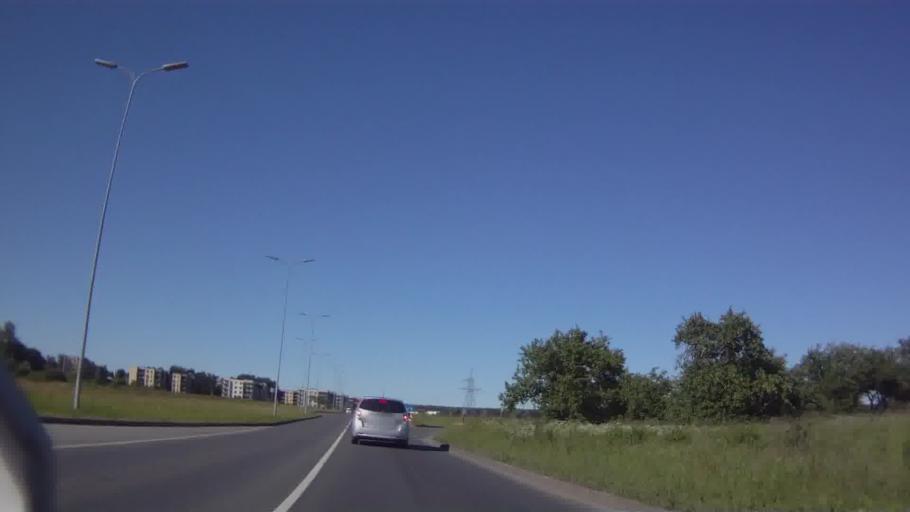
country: LV
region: Stopini
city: Ulbroka
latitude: 56.9457
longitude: 24.2450
